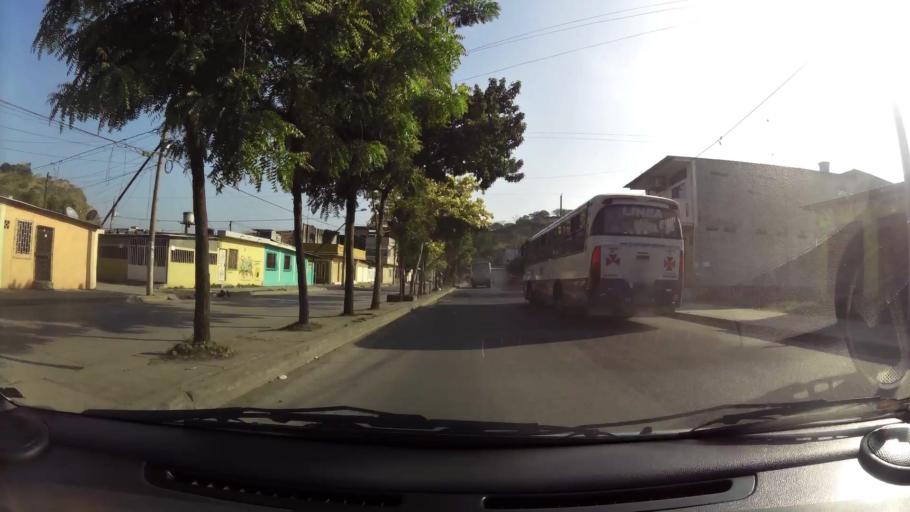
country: EC
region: Guayas
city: Eloy Alfaro
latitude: -2.1749
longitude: -79.8394
